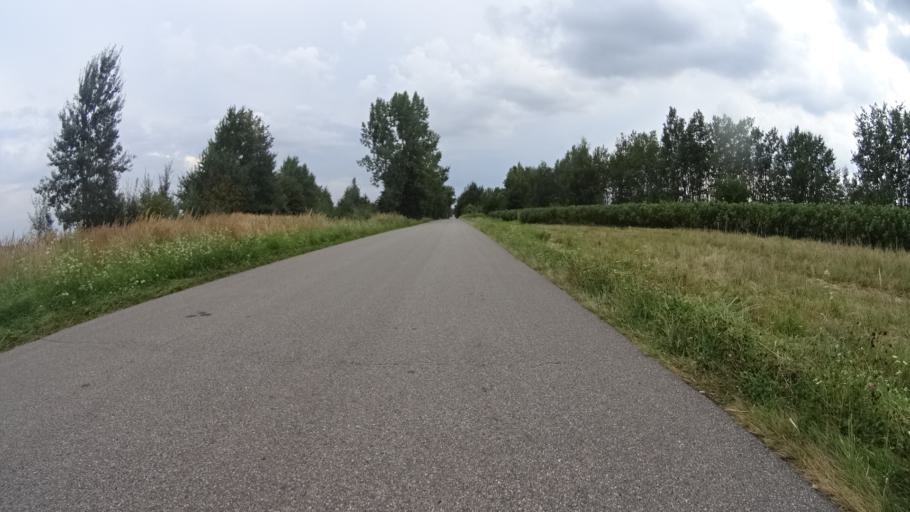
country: PL
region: Masovian Voivodeship
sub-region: Powiat grojecki
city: Goszczyn
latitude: 51.6793
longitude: 20.8598
